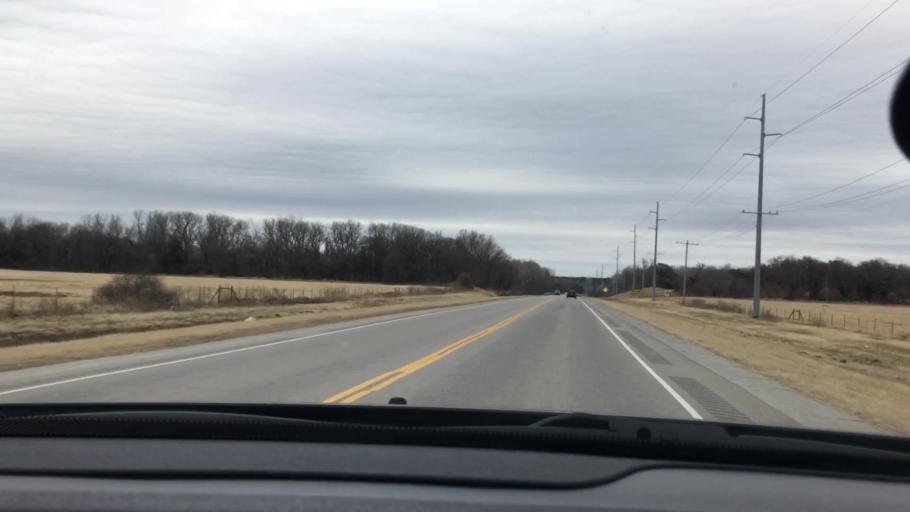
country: US
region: Oklahoma
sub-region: Marshall County
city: Oakland
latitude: 34.2135
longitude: -96.8022
